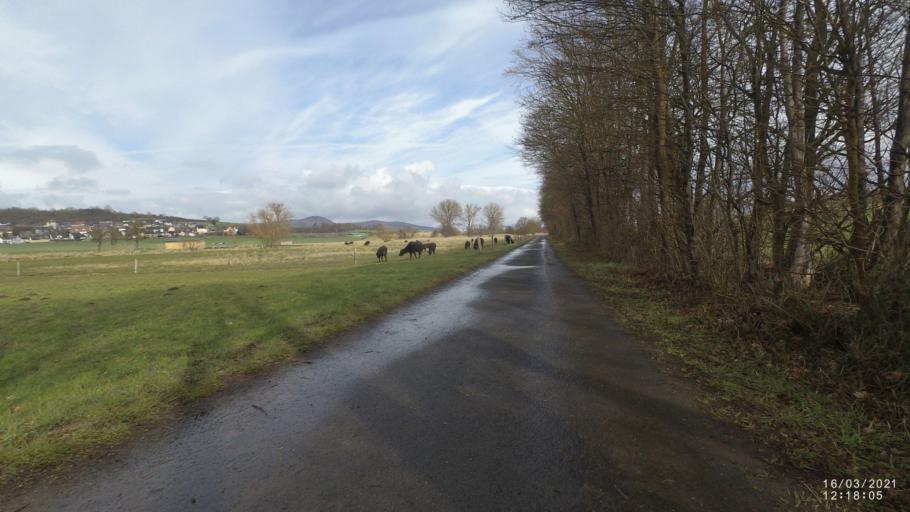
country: DE
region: Rheinland-Pfalz
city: Thur
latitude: 50.3515
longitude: 7.2859
